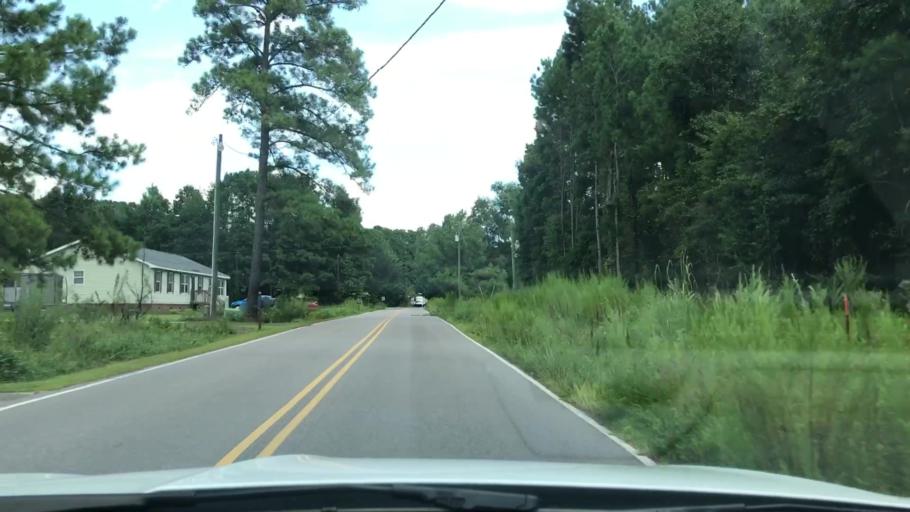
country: US
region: South Carolina
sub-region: Dorchester County
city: Summerville
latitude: 33.0338
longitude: -80.2111
